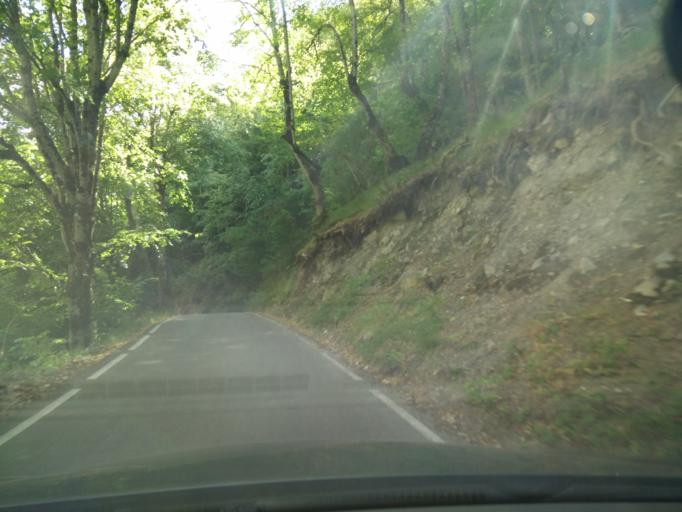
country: ES
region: Castille and Leon
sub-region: Provincia de Leon
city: Posada de Valdeon
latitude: 43.1857
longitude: -4.9044
